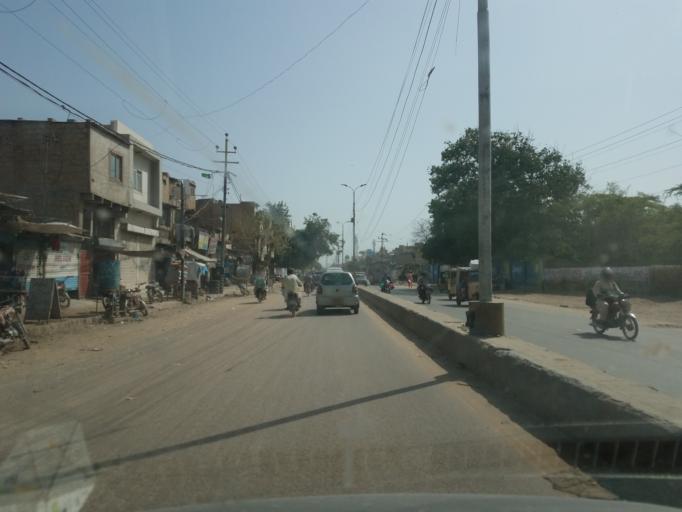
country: PK
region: Sindh
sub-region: Karachi District
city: Karachi
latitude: 24.8885
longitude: 67.0422
